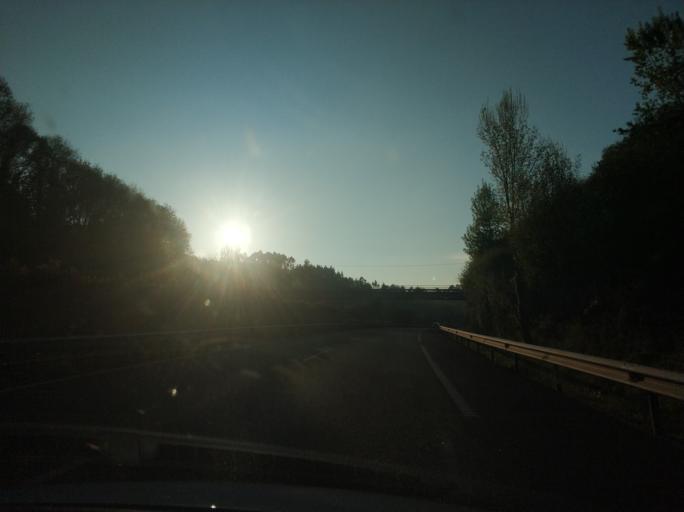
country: ES
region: Cantabria
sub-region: Provincia de Cantabria
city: Colindres
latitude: 43.3908
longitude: -3.4763
